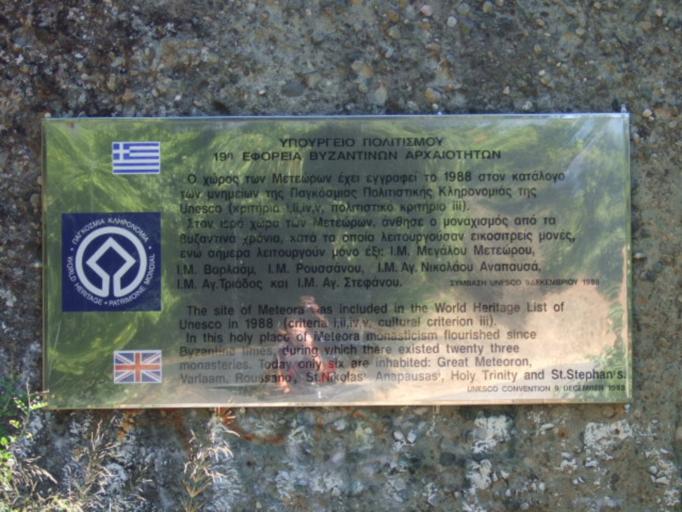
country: GR
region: Thessaly
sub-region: Trikala
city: Kastraki
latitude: 39.7218
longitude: 21.6222
